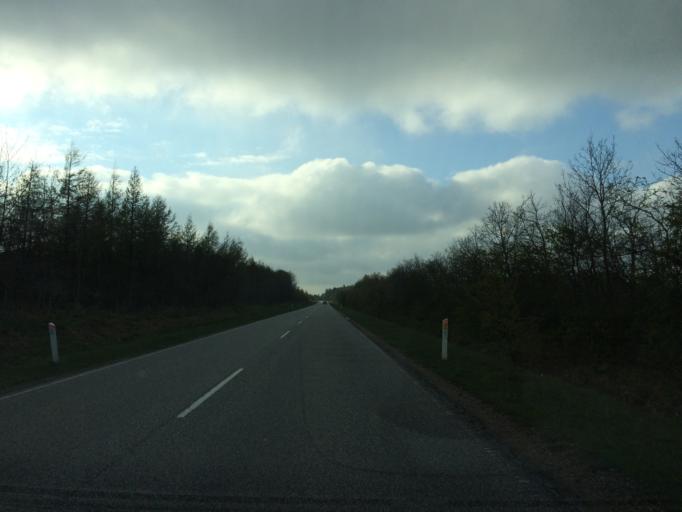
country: DK
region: Central Jutland
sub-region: Viborg Kommune
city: Karup
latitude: 56.3322
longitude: 9.0989
